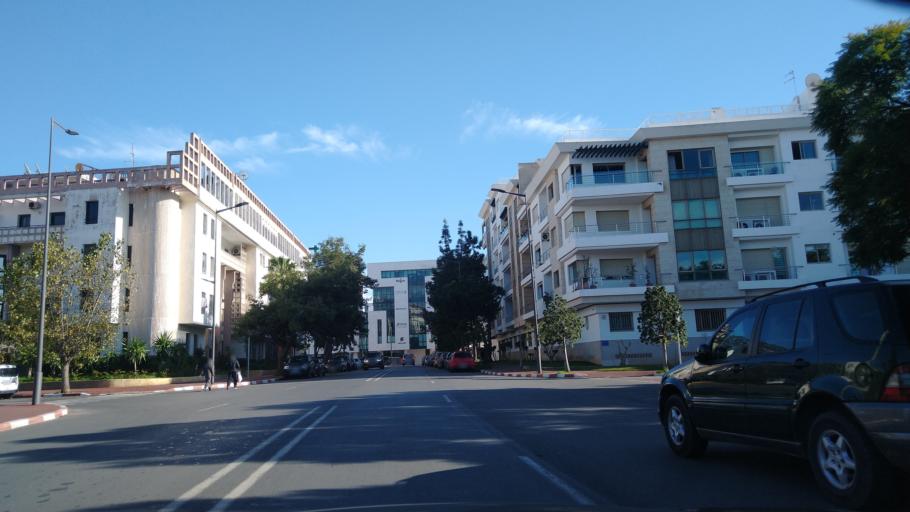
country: MA
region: Rabat-Sale-Zemmour-Zaer
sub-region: Skhirate-Temara
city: Temara
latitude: 33.9633
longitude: -6.8679
